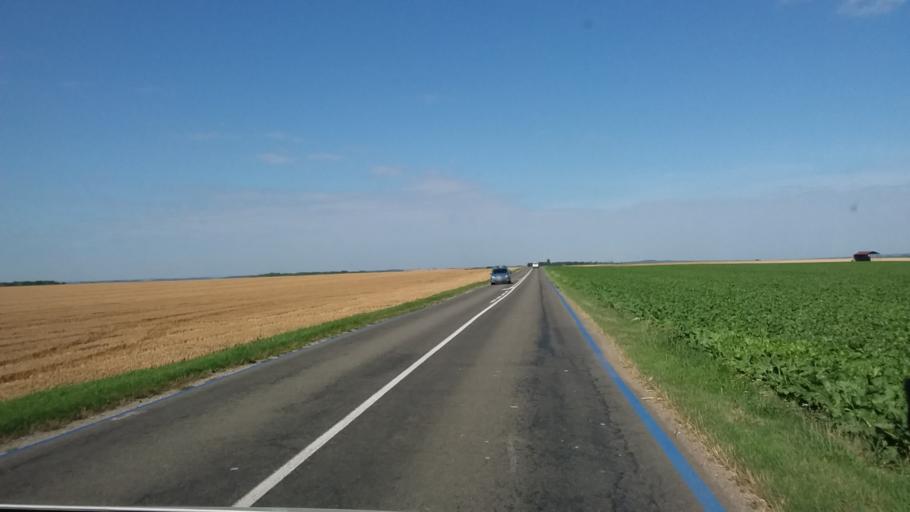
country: FR
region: Picardie
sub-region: Departement de l'Aisne
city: Bruyeres-et-Montberault
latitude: 49.4403
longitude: 3.7066
